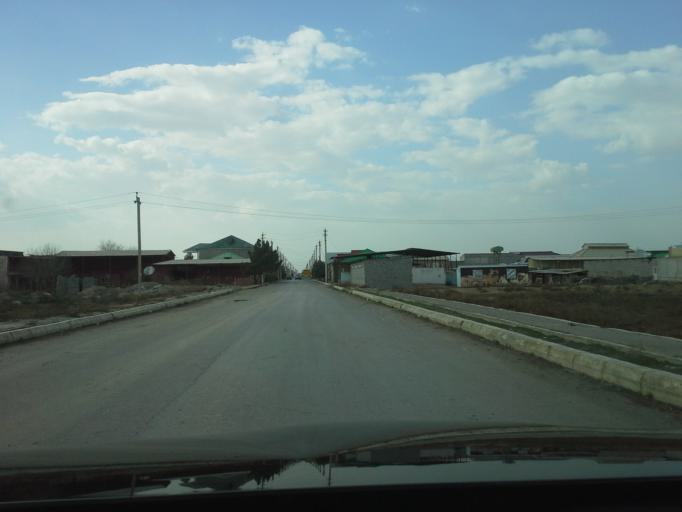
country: TM
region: Ahal
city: Ashgabat
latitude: 37.9888
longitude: 58.2967
